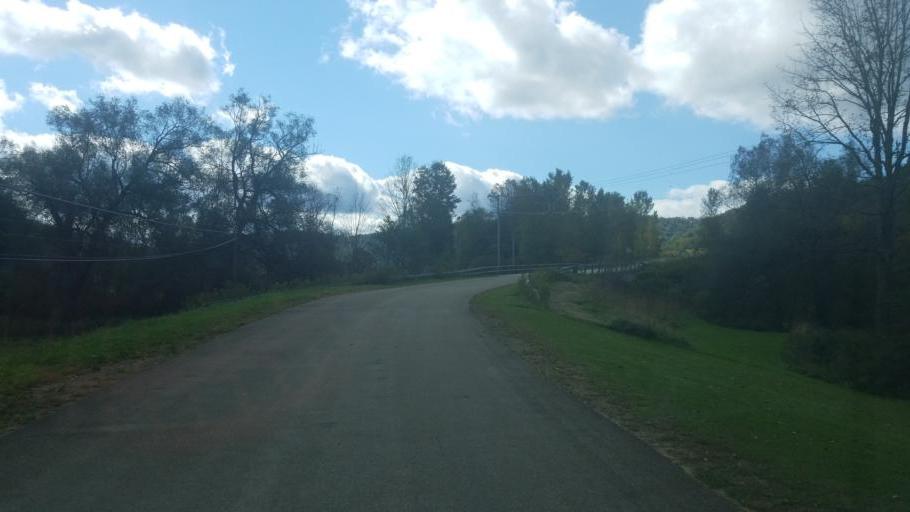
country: US
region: New York
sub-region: Cattaraugus County
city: Franklinville
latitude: 42.2437
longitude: -78.3974
